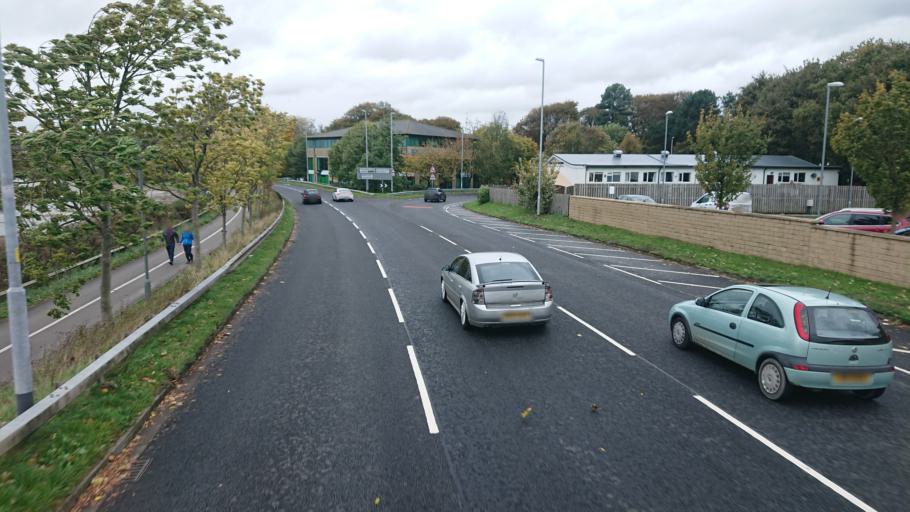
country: GB
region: England
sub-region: Lancashire
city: Lancaster
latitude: 54.0543
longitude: -2.8033
